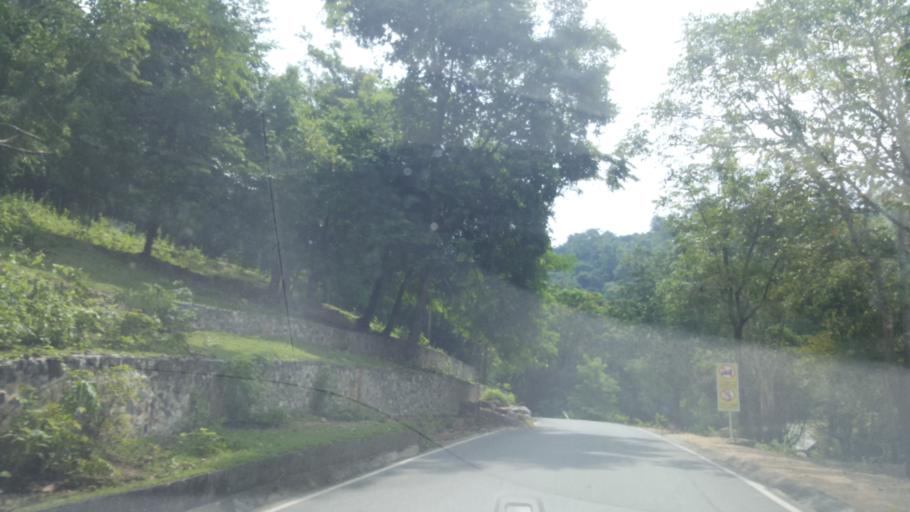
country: TH
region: Chon Buri
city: Ban Bueng
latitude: 13.2119
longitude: 101.0662
